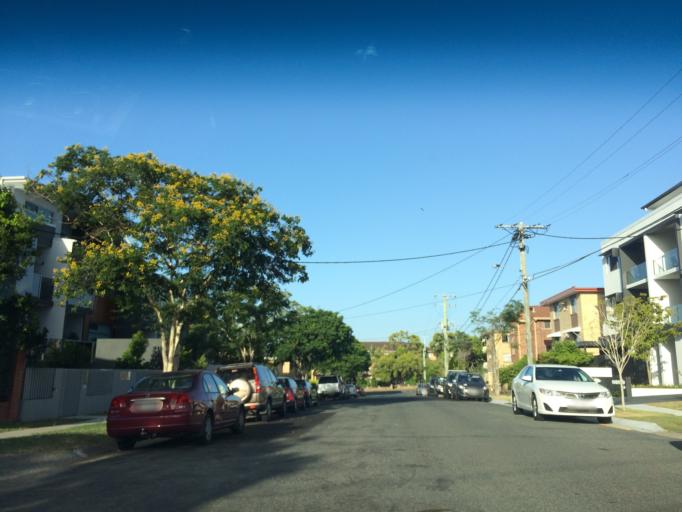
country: AU
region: Queensland
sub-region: Brisbane
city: Camp Hill
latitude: -27.4922
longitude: 153.0586
